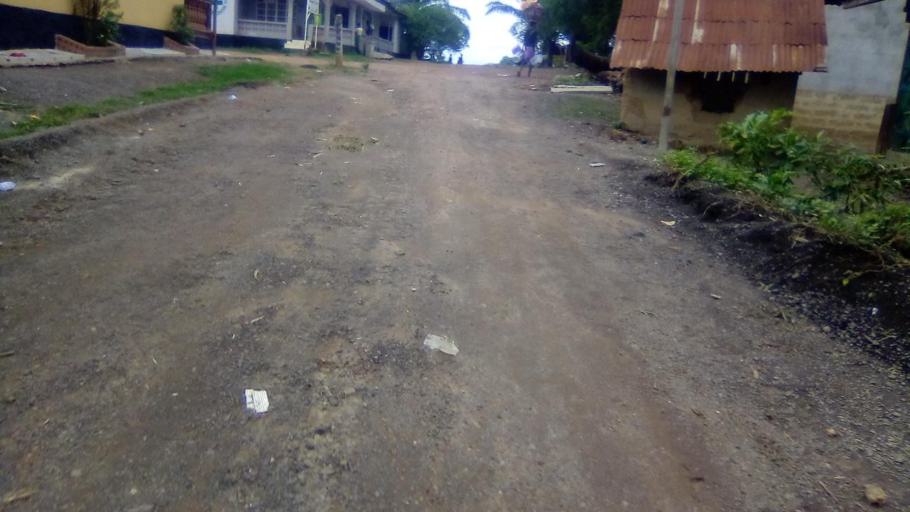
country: SL
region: Southern Province
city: Bo
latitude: 7.9424
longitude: -11.7420
